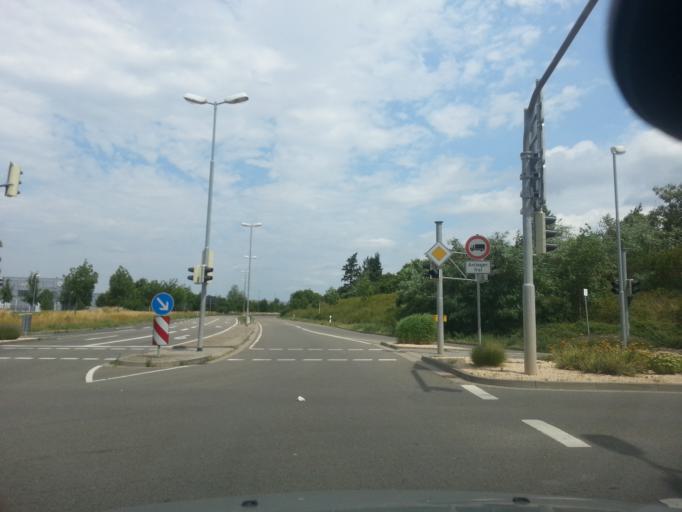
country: DE
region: Rheinland-Pfalz
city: Frankenthal
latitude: 49.5415
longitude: 8.3368
